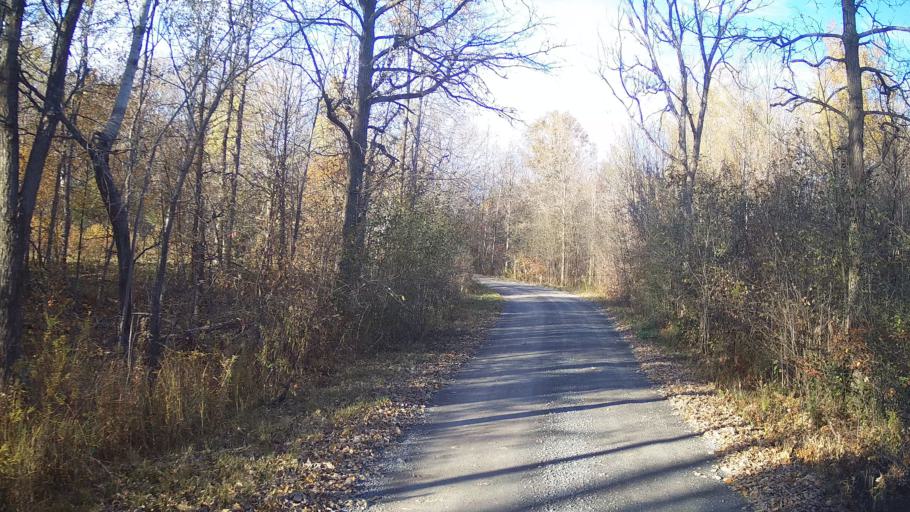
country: CA
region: Ontario
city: Perth
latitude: 44.7216
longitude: -76.4384
